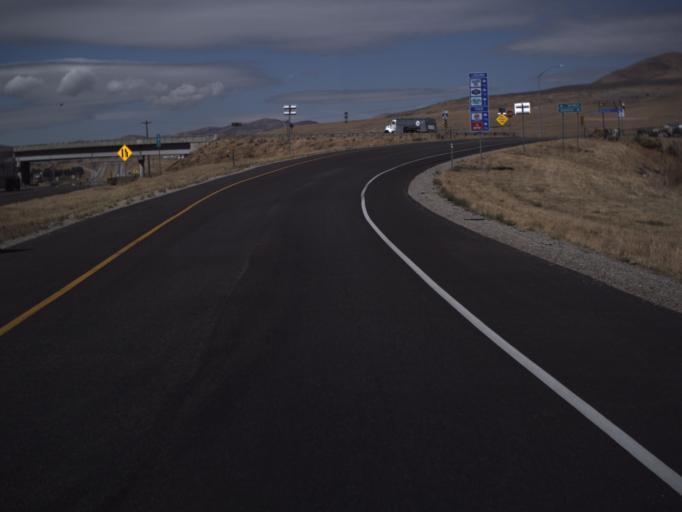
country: US
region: Utah
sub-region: Box Elder County
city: Tremonton
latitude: 41.7096
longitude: -112.2025
